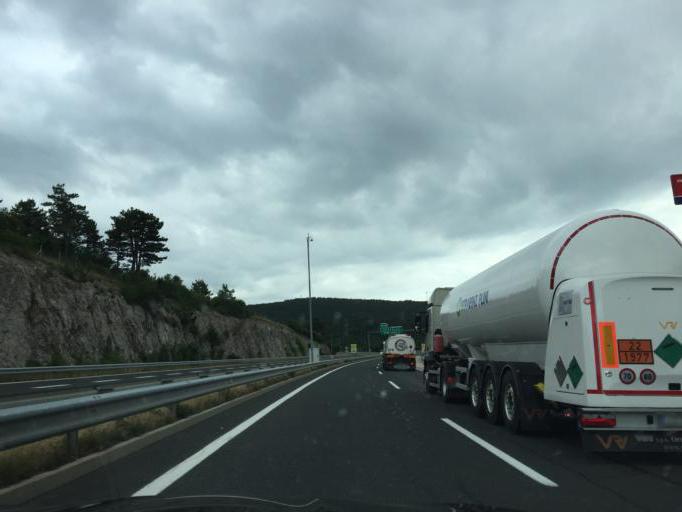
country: SI
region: Hrpelje-Kozina
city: Kozina
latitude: 45.6047
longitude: 13.9279
